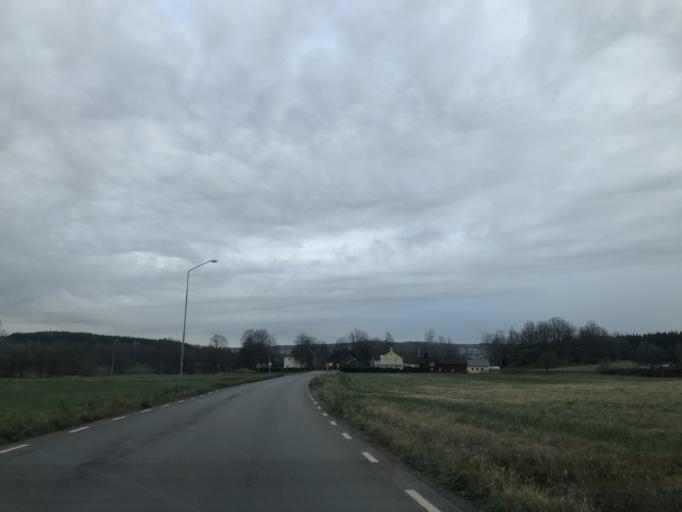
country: SE
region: Vaestra Goetaland
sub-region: Ulricehamns Kommun
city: Ulricehamn
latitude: 57.7983
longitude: 13.3691
